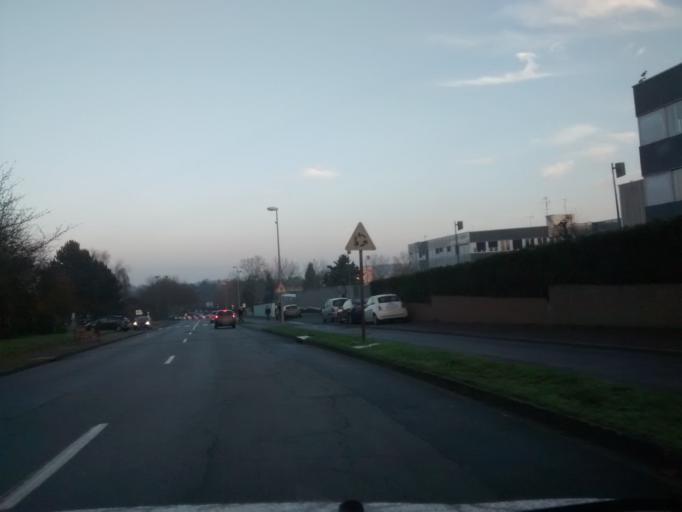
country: FR
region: Brittany
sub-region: Departement d'Ille-et-Vilaine
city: Cesson-Sevigne
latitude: 48.1256
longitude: -1.6280
